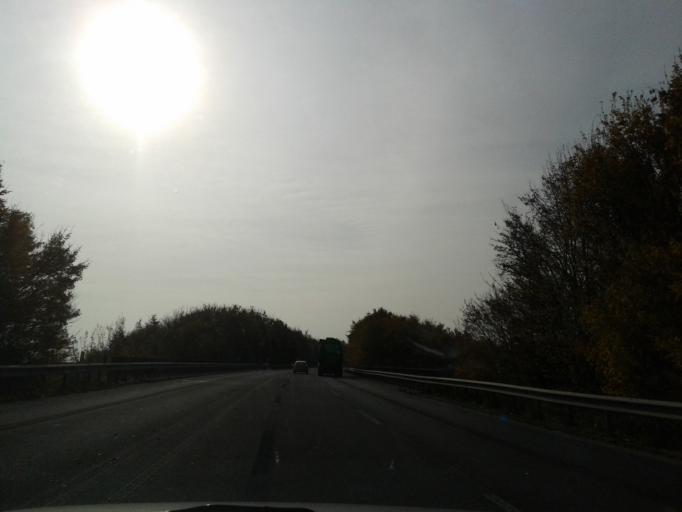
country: DE
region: North Rhine-Westphalia
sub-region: Regierungsbezirk Arnsberg
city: Ruthen
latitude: 51.5229
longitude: 8.4566
